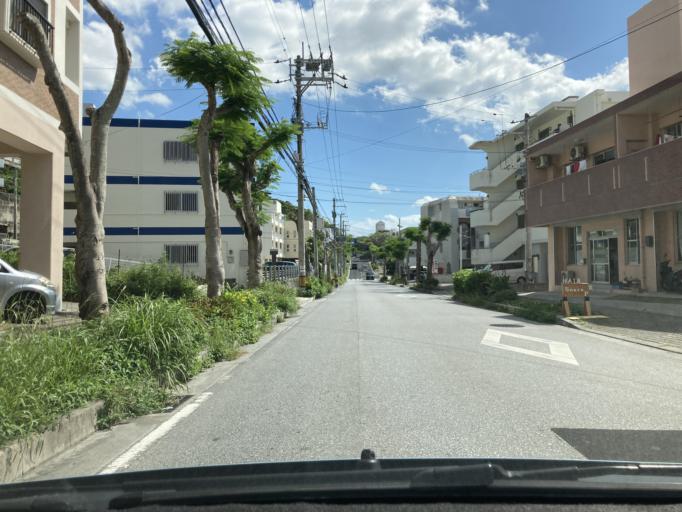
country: JP
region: Okinawa
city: Tomigusuku
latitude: 26.1990
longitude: 127.6987
